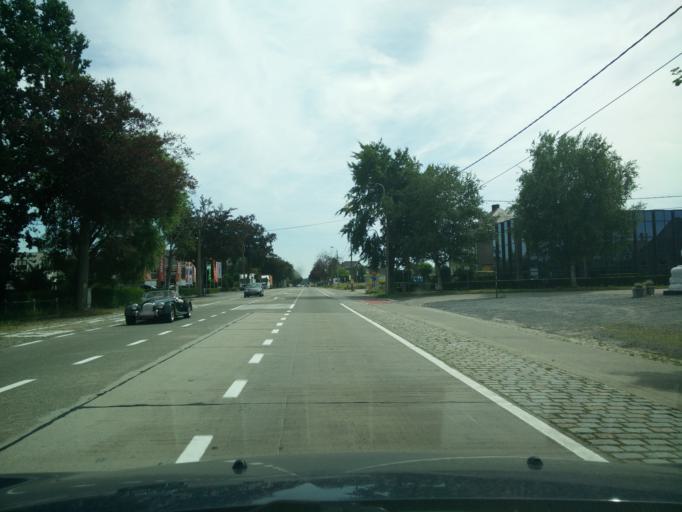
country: BE
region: Flanders
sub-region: Provincie Oost-Vlaanderen
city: Melle
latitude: 51.0194
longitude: 3.7795
